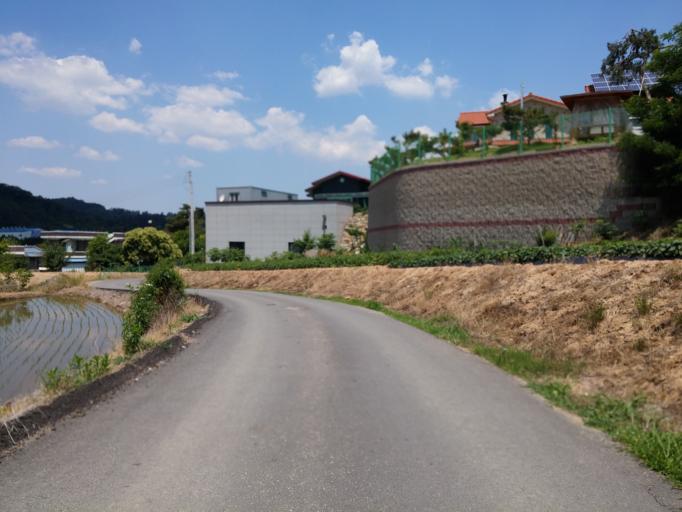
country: KR
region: Chungcheongbuk-do
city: Cheongju-si
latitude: 36.5541
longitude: 127.4353
